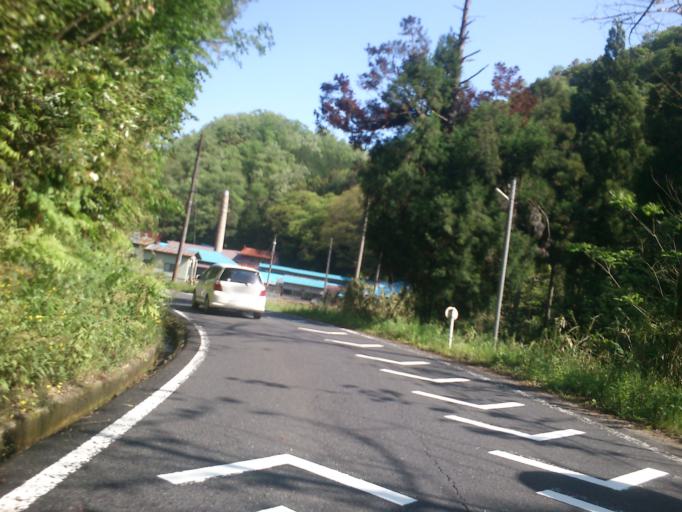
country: JP
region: Kyoto
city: Miyazu
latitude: 35.5788
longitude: 135.1616
